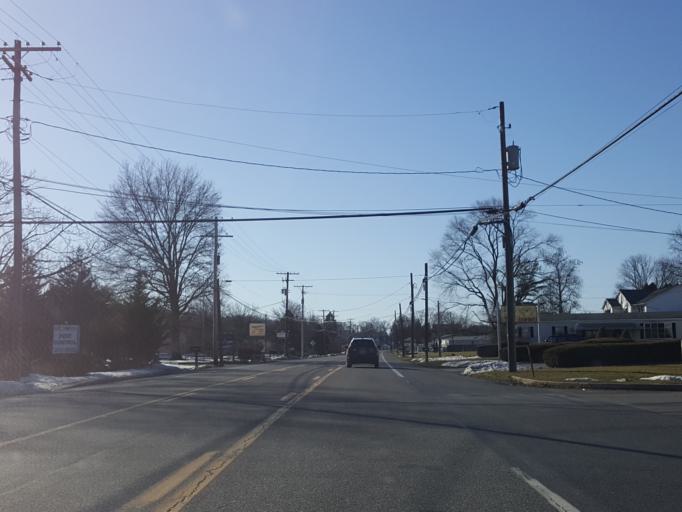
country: US
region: Pennsylvania
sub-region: Lancaster County
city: Mountville
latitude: 40.0371
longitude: -76.4125
